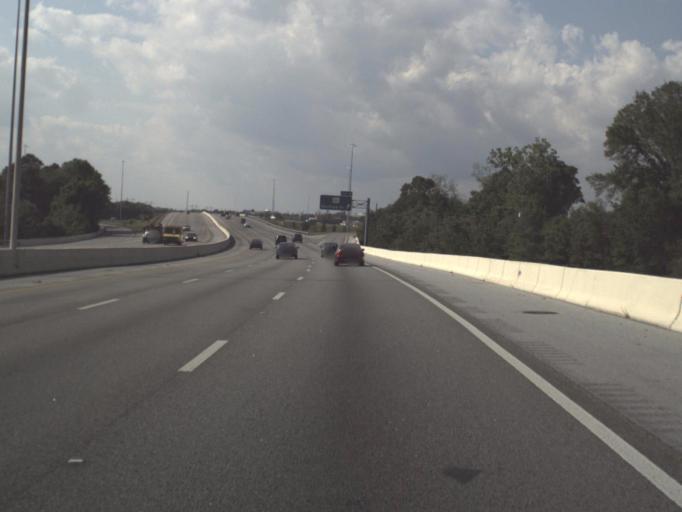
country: US
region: Florida
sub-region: Escambia County
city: Goulding
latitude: 30.4476
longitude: -87.2183
